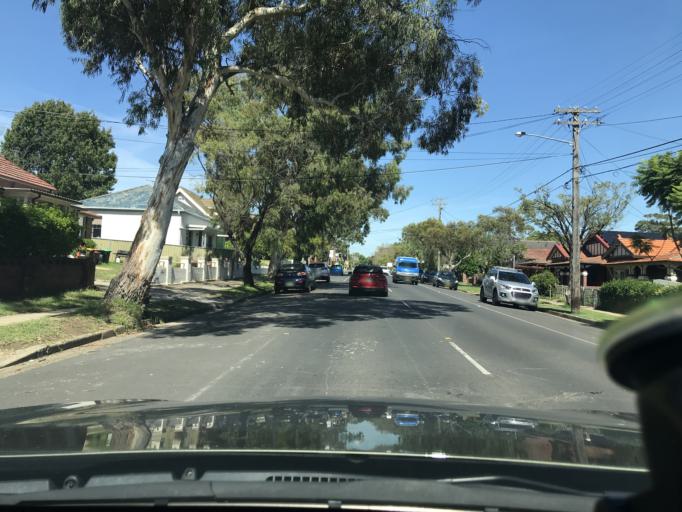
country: AU
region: New South Wales
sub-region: Canada Bay
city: Concord
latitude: -33.8605
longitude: 151.1068
